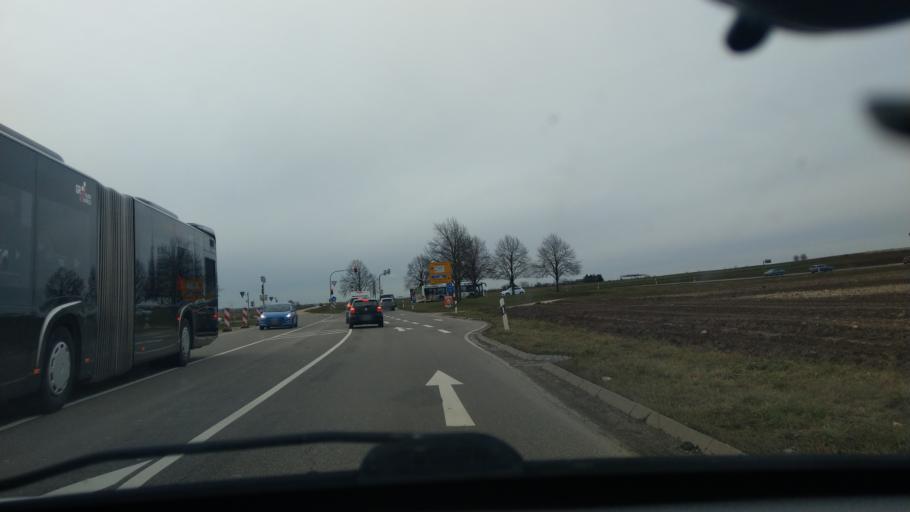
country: DE
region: Baden-Wuerttemberg
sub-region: Regierungsbezirk Stuttgart
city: Neuhausen auf den Fildern
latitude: 48.6916
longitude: 9.2658
